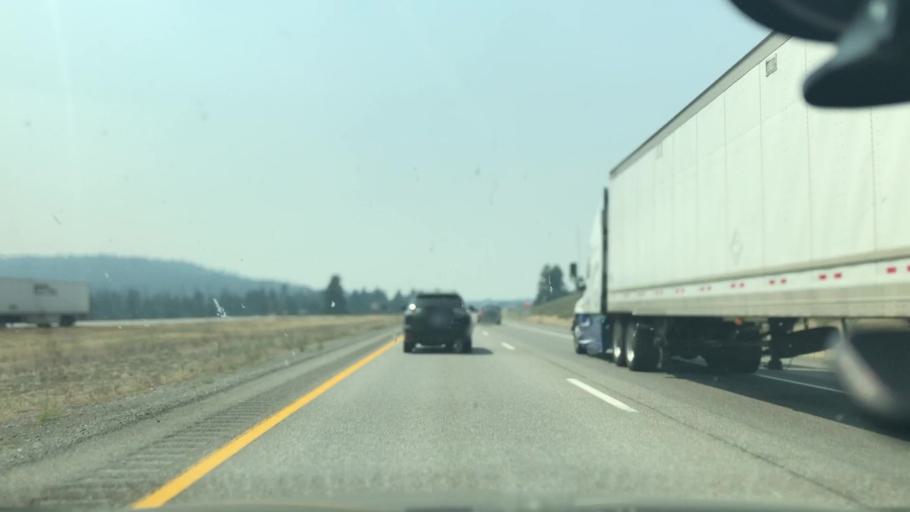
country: US
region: Washington
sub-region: Spokane County
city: Otis Orchards-East Farms
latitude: 47.6985
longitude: -117.0313
